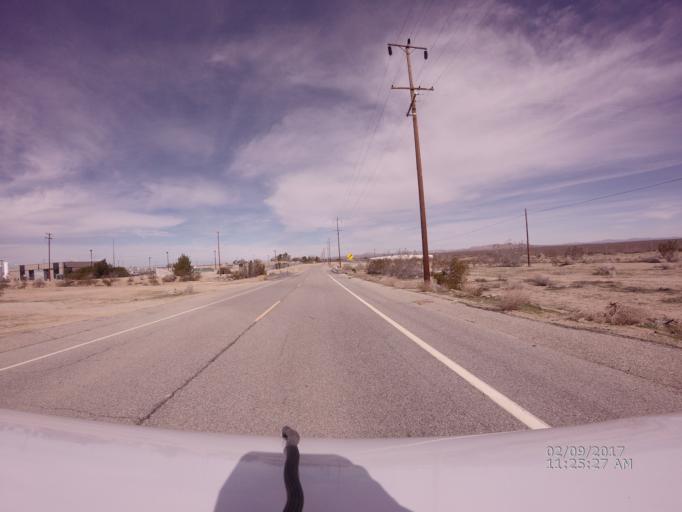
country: US
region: California
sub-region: Los Angeles County
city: Littlerock
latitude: 34.5217
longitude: -117.9231
